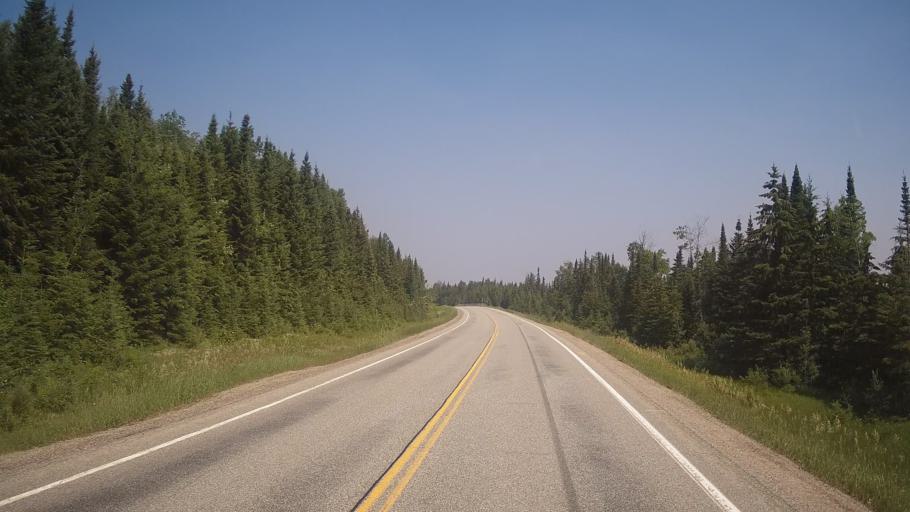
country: CA
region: Ontario
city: Timmins
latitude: 48.1705
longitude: -81.5826
